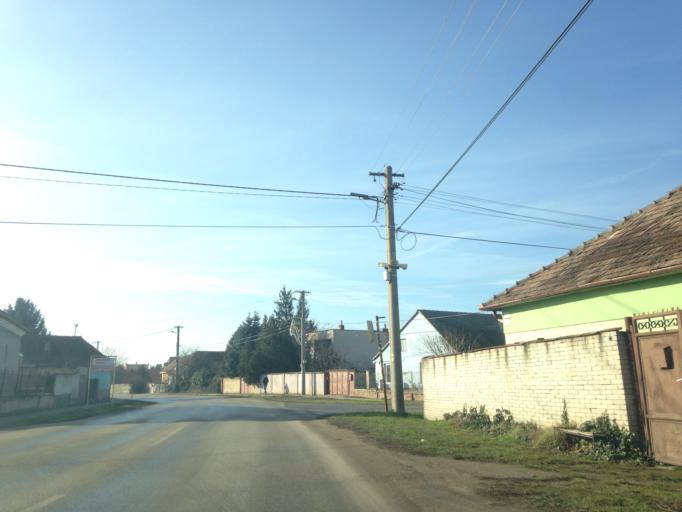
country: SK
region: Nitriansky
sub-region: Okres Nove Zamky
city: Nove Zamky
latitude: 47.9969
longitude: 18.2666
